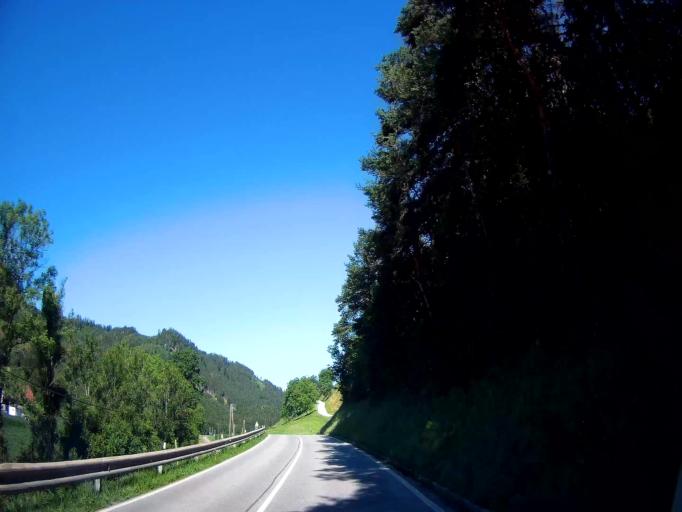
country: AT
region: Carinthia
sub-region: Politischer Bezirk Sankt Veit an der Glan
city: Bruckl
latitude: 46.7538
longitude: 14.5048
